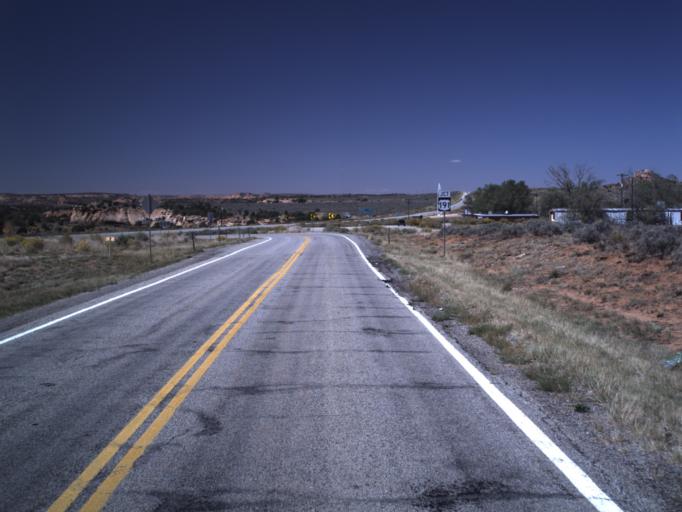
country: US
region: Utah
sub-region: Grand County
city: Moab
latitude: 38.3089
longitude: -109.4012
